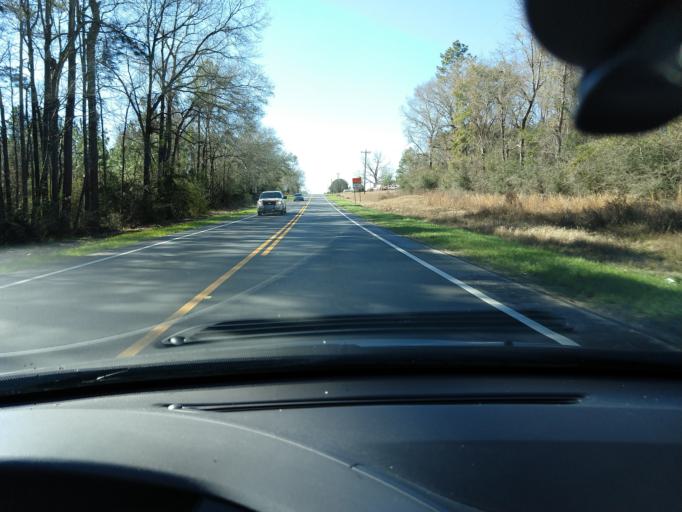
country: US
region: Alabama
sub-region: Covington County
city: Andalusia
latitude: 31.2088
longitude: -86.5462
